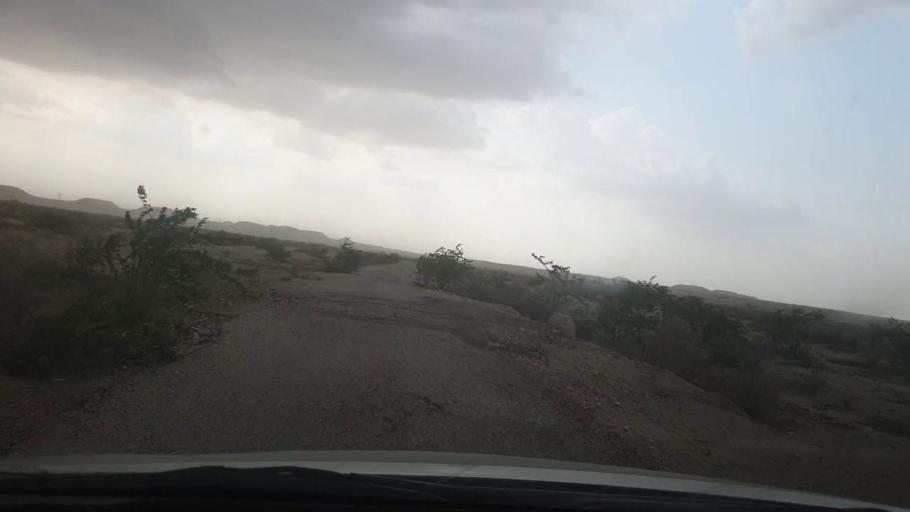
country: PK
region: Sindh
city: Khairpur
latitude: 27.4408
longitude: 68.9769
